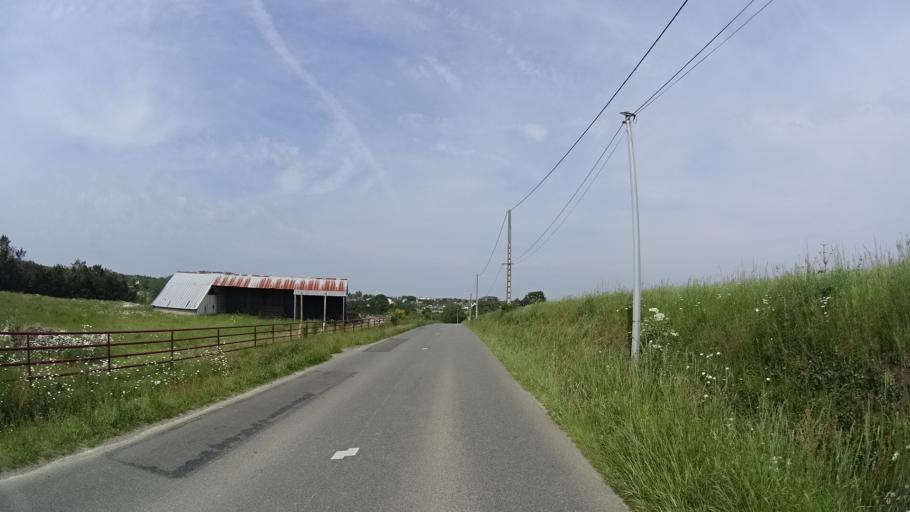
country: FR
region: Brittany
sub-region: Departement d'Ille-et-Vilaine
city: Bourgbarre
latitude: 47.9917
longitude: -1.5983
